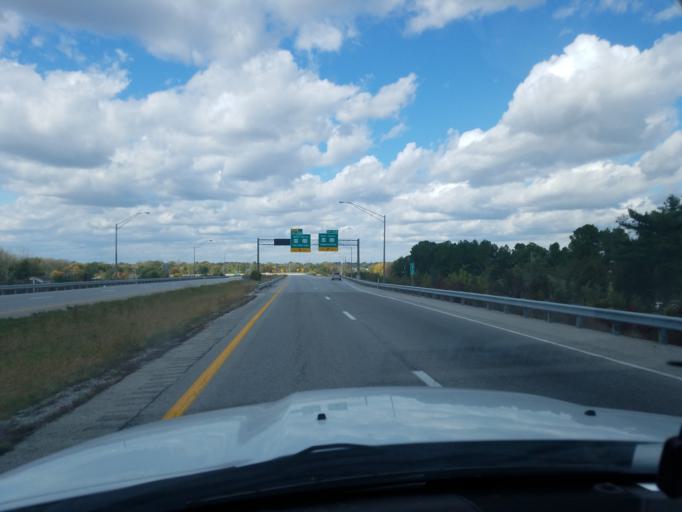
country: US
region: Kentucky
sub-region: Daviess County
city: Owensboro
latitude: 37.7373
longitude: -87.0695
